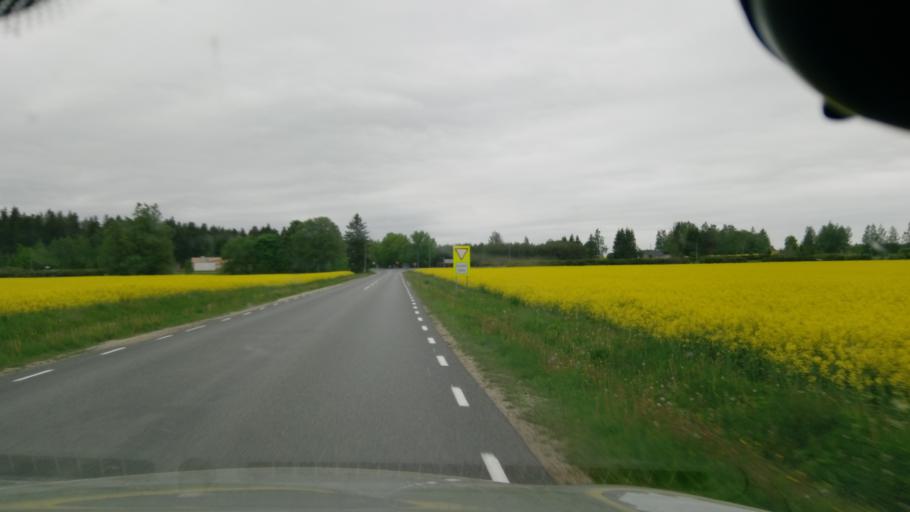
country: EE
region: Jaervamaa
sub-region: Koeru vald
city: Koeru
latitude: 58.9841
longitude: 26.0490
